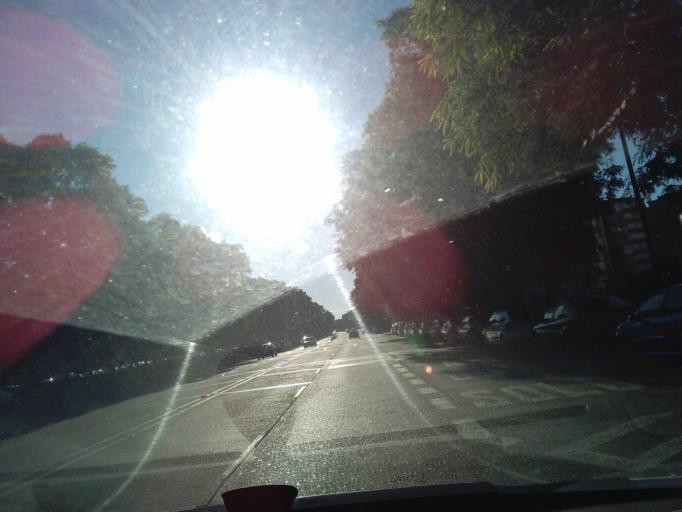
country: ES
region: Andalusia
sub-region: Provincia de Sevilla
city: Sevilla
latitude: 37.3730
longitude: -5.9653
